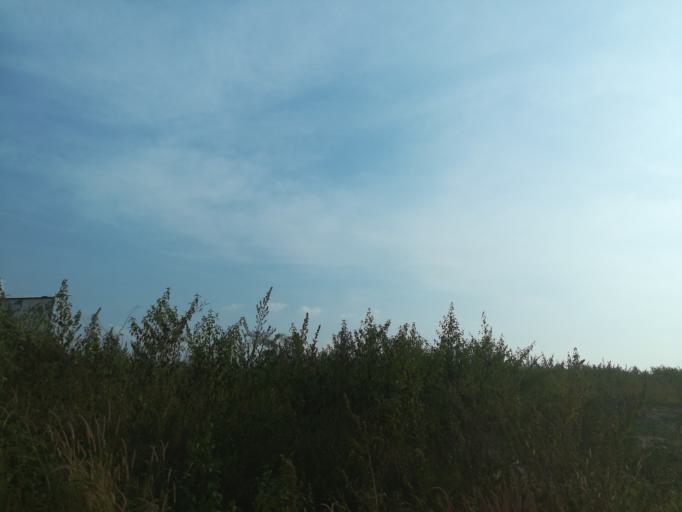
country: NG
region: Abuja Federal Capital Territory
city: Abuja
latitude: 9.0908
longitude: 7.3736
